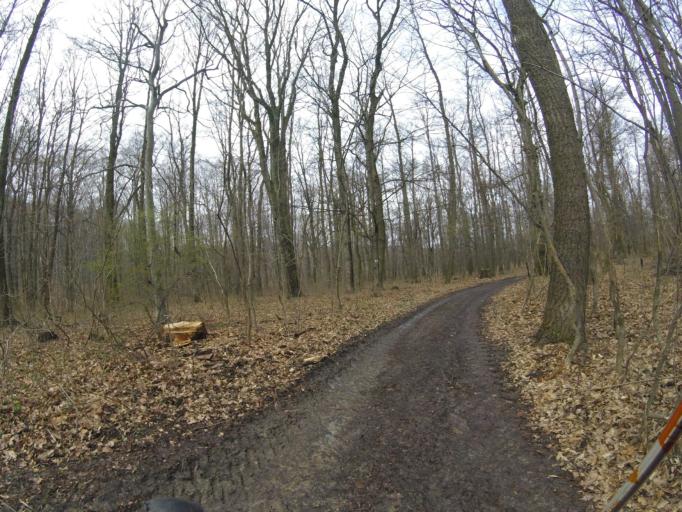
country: HU
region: Veszprem
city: Zirc
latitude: 47.3310
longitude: 17.9067
